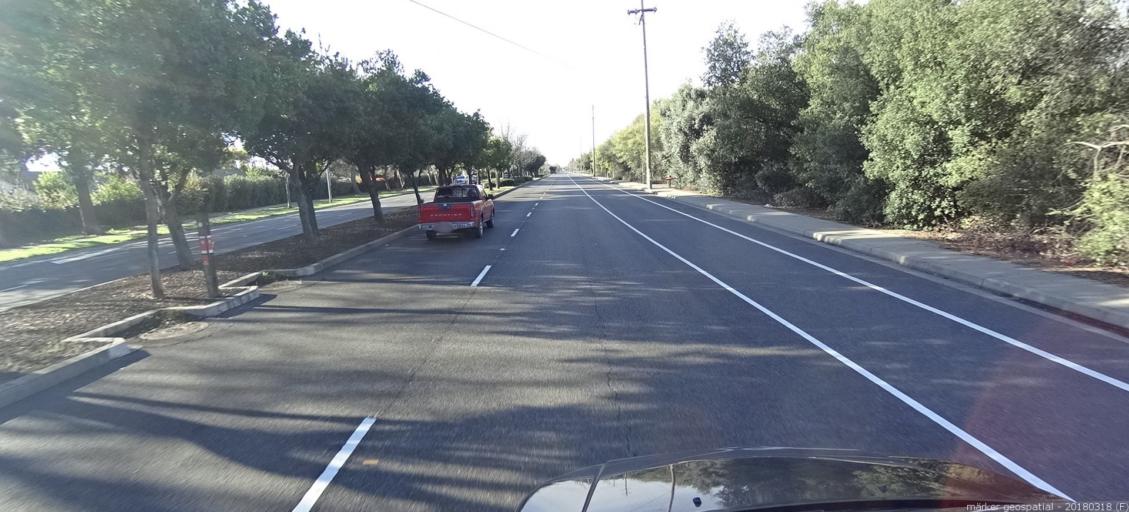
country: US
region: California
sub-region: Sacramento County
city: Laguna
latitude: 38.4408
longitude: -121.4453
